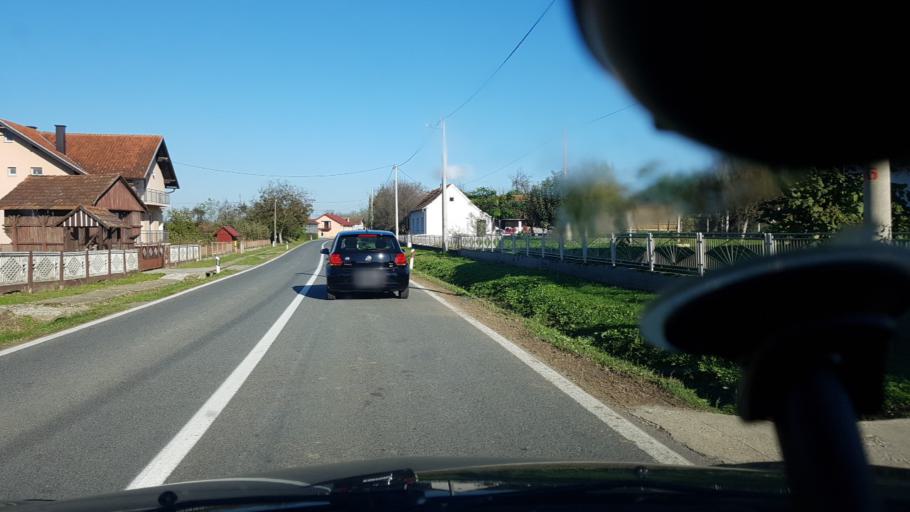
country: HR
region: Bjelovarsko-Bilogorska
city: Gudovac
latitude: 45.8326
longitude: 16.7980
